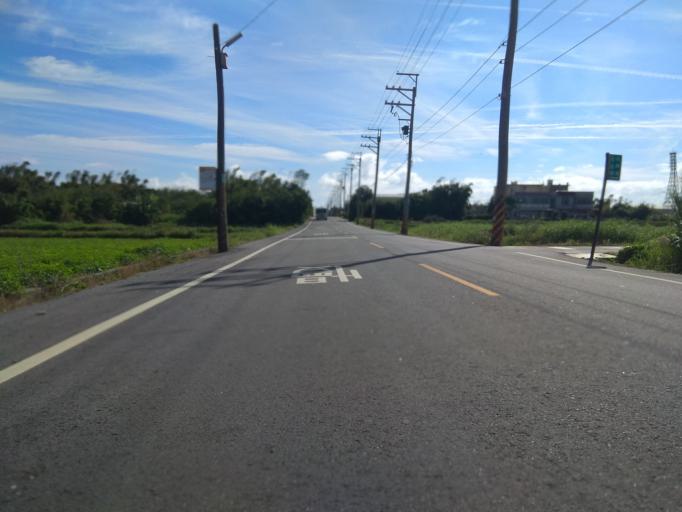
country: TW
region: Taiwan
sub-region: Hsinchu
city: Zhubei
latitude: 25.0101
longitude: 121.0404
